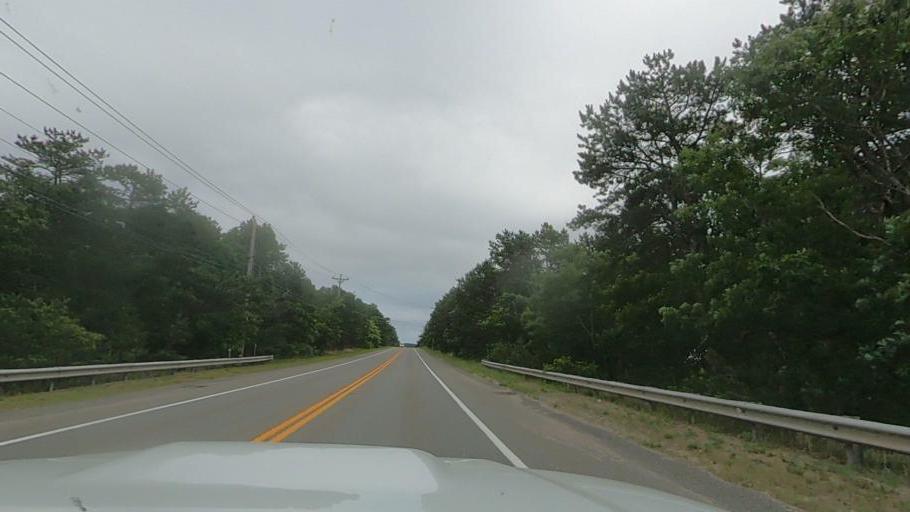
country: US
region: Massachusetts
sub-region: Barnstable County
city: Truro
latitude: 41.9777
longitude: -70.0393
